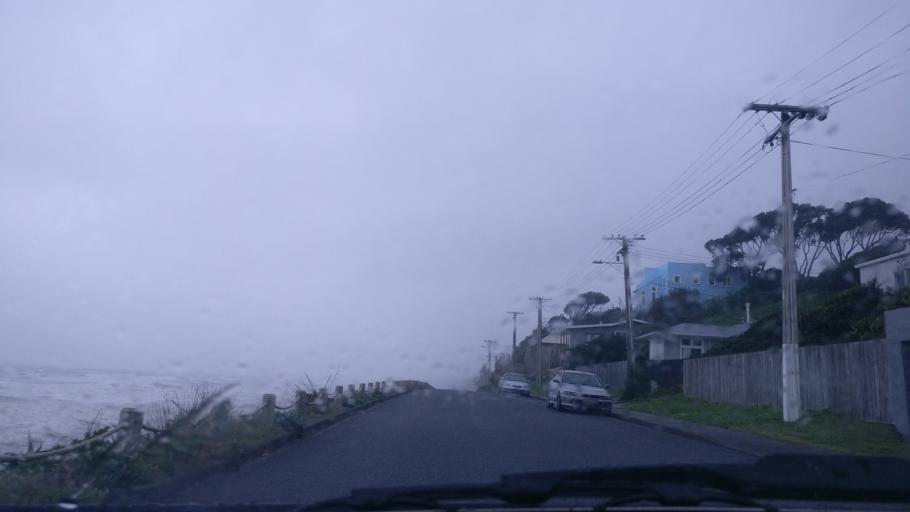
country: NZ
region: Wellington
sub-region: Kapiti Coast District
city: Paraparaumu
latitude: -40.9868
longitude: 174.9502
